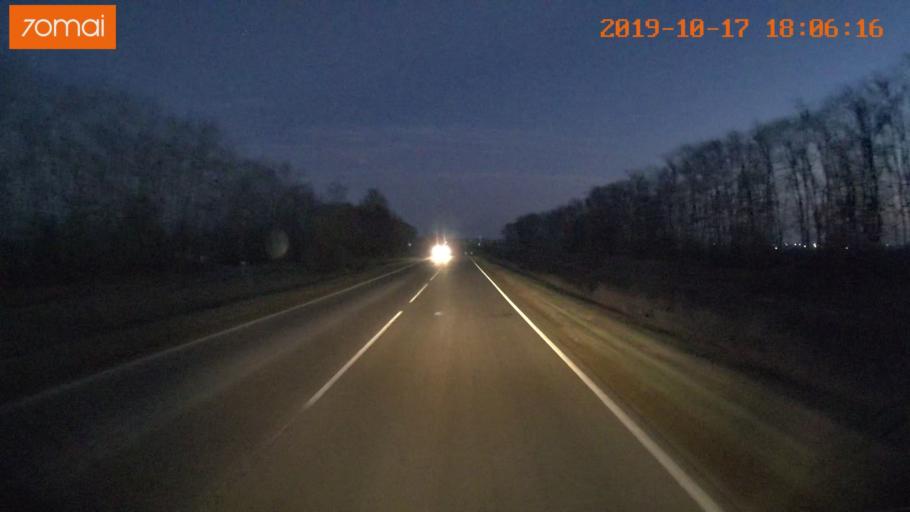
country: RU
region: Tula
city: Kurkino
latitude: 53.4546
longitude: 38.6531
